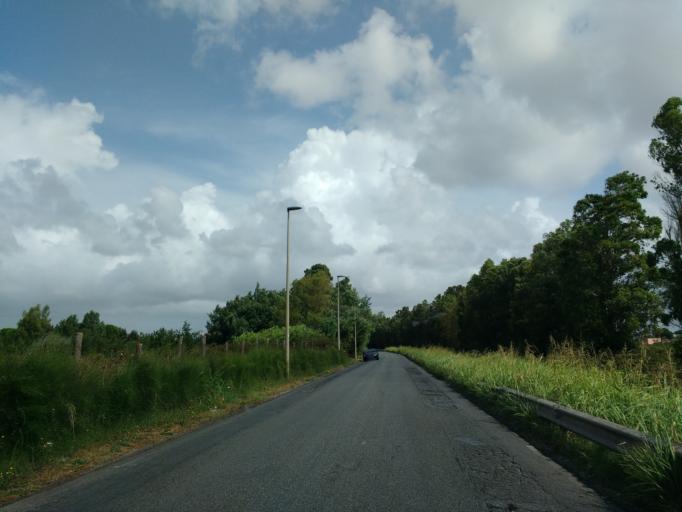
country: IT
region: Latium
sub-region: Citta metropolitana di Roma Capitale
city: Acilia-Castel Fusano-Ostia Antica
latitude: 41.7576
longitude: 12.3299
